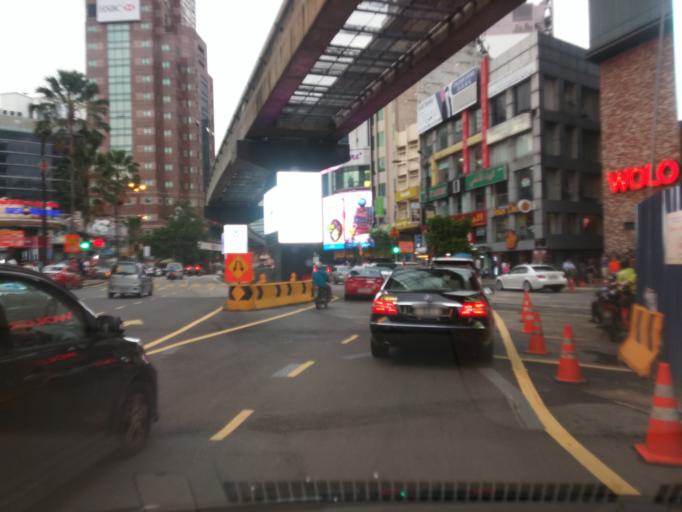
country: MY
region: Kuala Lumpur
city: Kuala Lumpur
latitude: 3.1469
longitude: 101.7112
